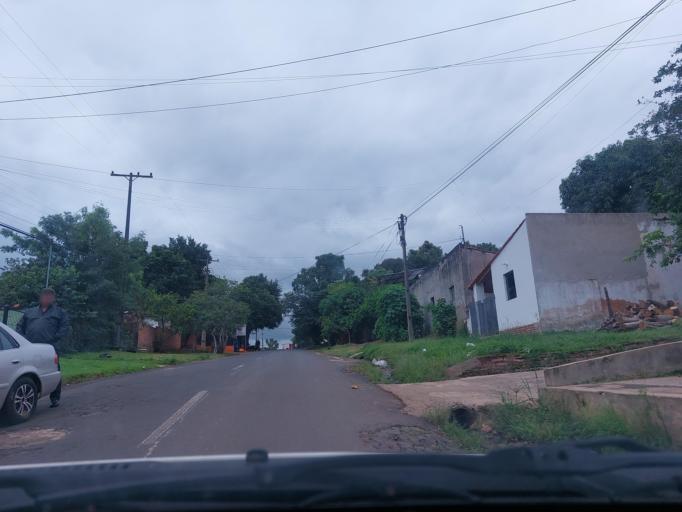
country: PY
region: San Pedro
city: Guayaybi
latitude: -24.6587
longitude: -56.4439
